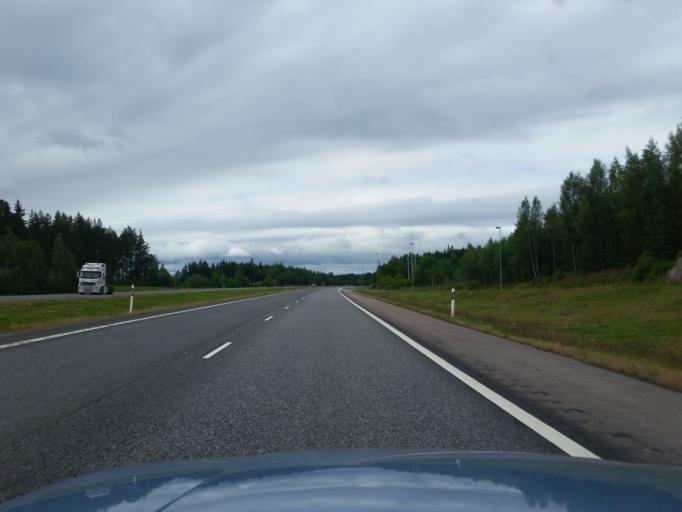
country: FI
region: Varsinais-Suomi
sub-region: Turku
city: Piikkioe
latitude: 60.4291
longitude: 22.4426
